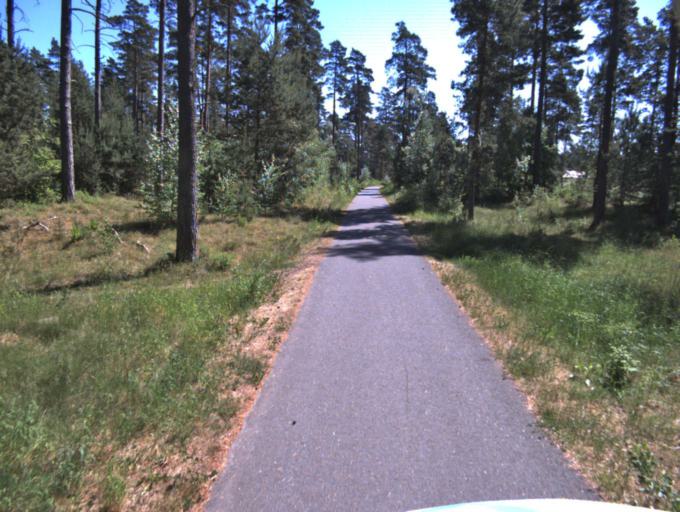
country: SE
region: Skane
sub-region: Kristianstads Kommun
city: Ahus
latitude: 55.9459
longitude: 14.2916
